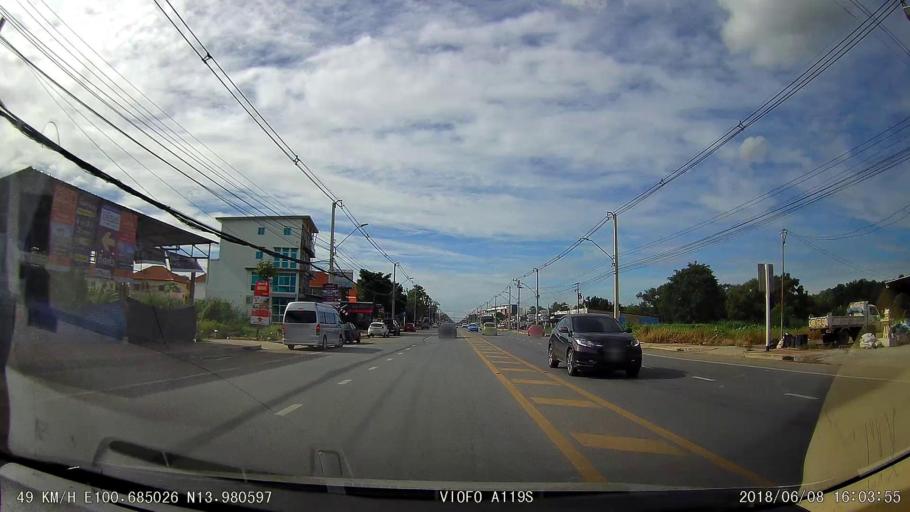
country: TH
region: Pathum Thani
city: Thanyaburi
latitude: 13.9806
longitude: 100.6850
